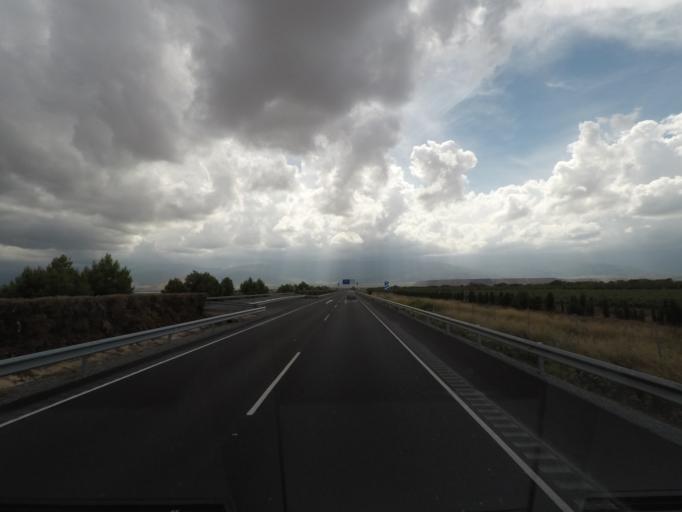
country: ES
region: Andalusia
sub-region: Provincia de Granada
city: Albunan
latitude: 37.2377
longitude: -3.0822
